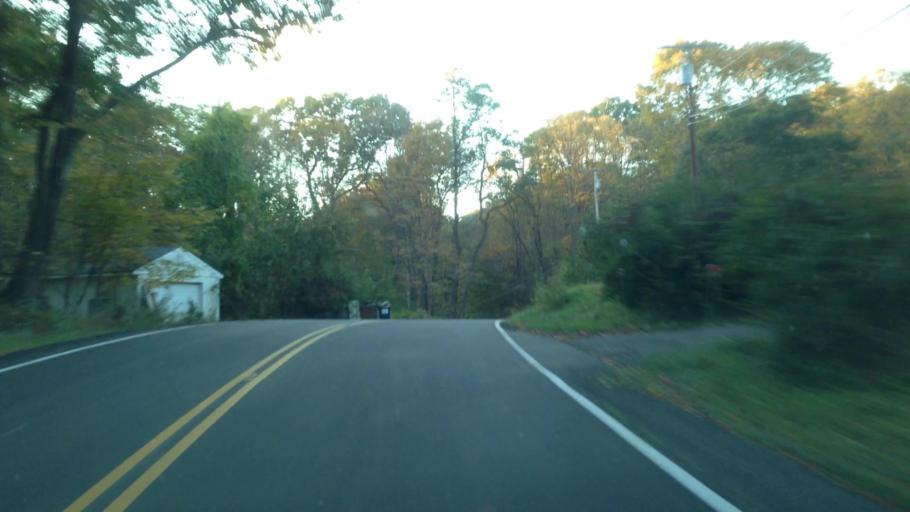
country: US
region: New York
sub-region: Ulster County
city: Tillson
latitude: 41.8248
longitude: -74.0041
